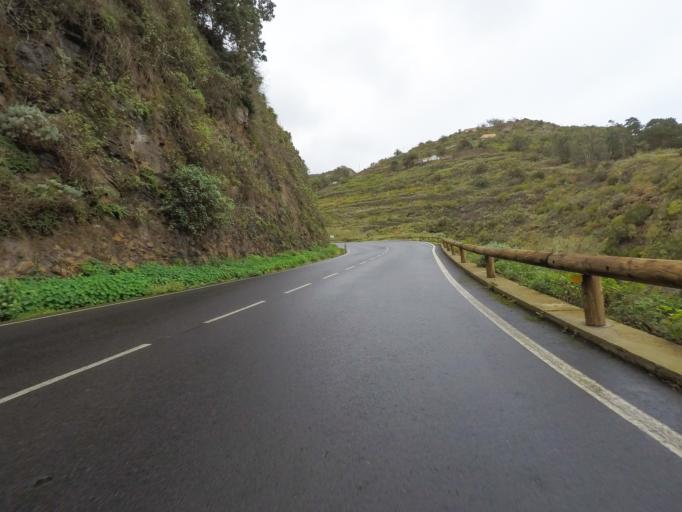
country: ES
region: Canary Islands
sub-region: Provincia de Santa Cruz de Tenerife
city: Agulo
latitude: 28.1861
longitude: -17.2188
